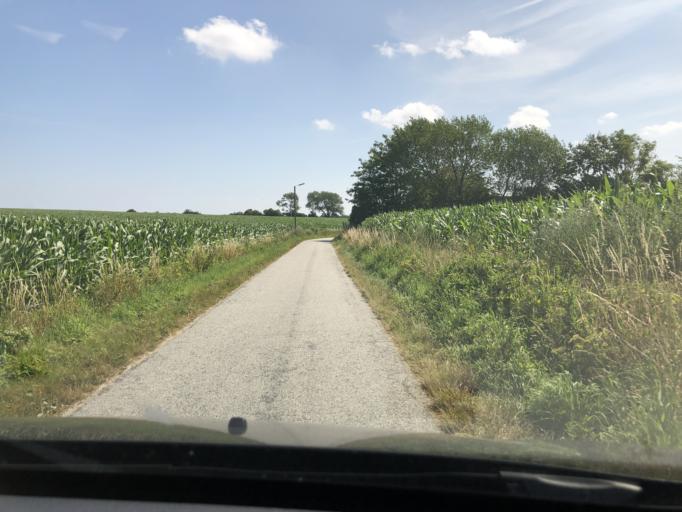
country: DK
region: South Denmark
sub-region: AEro Kommune
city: AEroskobing
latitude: 54.9148
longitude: 10.3172
